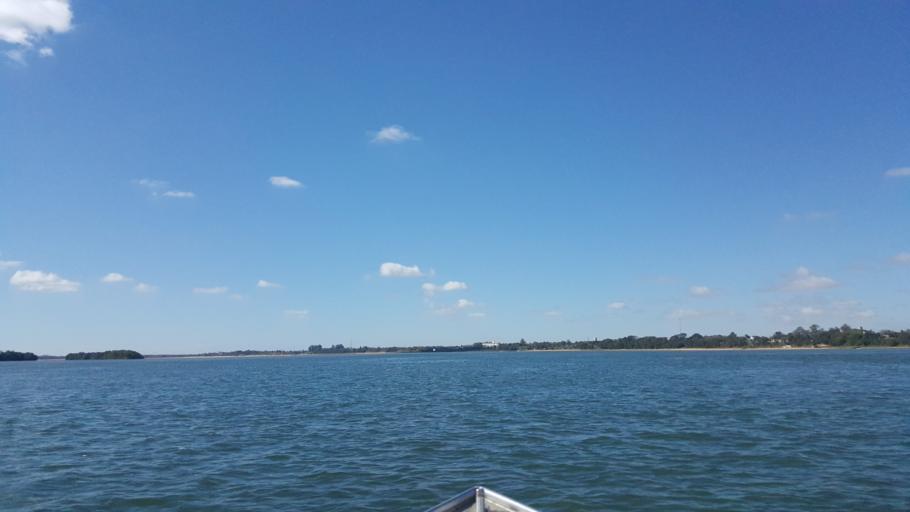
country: AR
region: Corrientes
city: Ituzaingo
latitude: -27.5818
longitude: -56.7018
